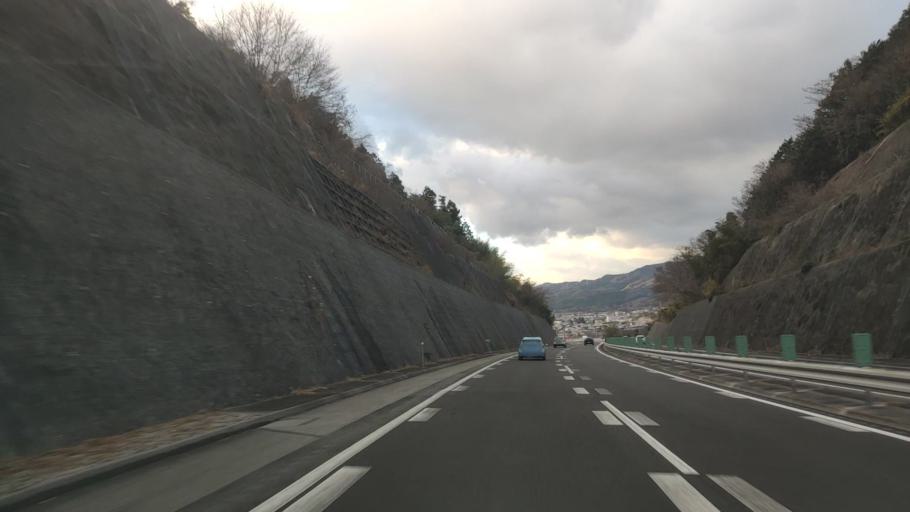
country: JP
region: Ehime
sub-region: Shikoku-chuo Shi
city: Matsuyama
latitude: 33.7915
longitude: 132.9145
